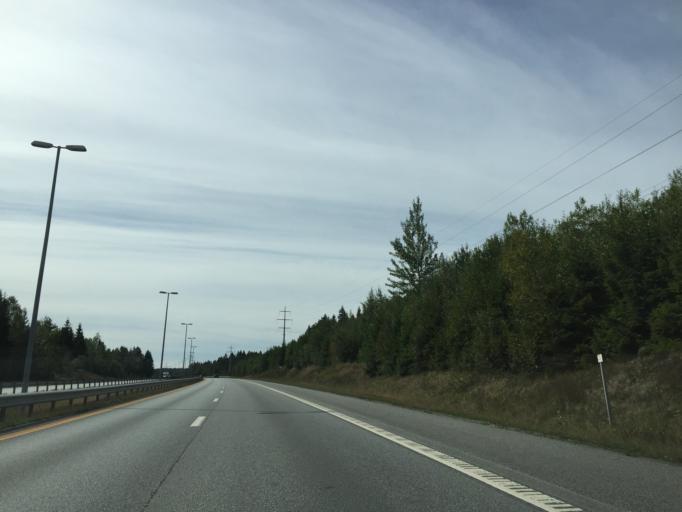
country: NO
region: Akershus
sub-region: Vestby
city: Vestby
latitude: 59.5686
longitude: 10.7220
